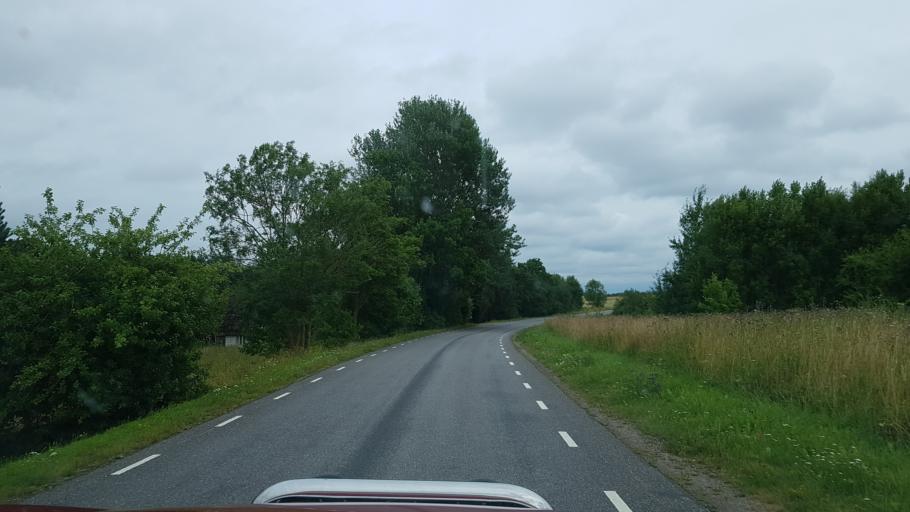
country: EE
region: Ida-Virumaa
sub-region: Puessi linn
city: Pussi
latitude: 59.3975
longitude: 27.0157
